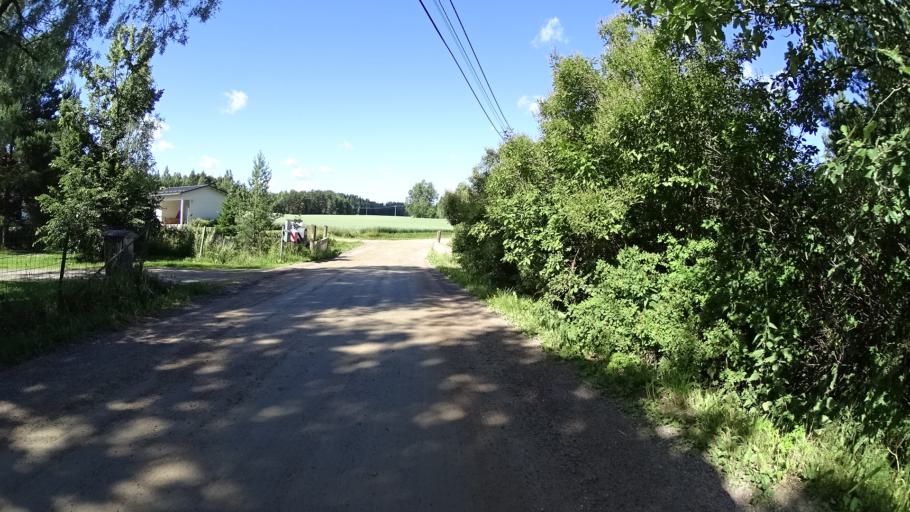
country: FI
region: Uusimaa
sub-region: Helsinki
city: Jaervenpaeae
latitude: 60.4375
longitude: 25.0744
